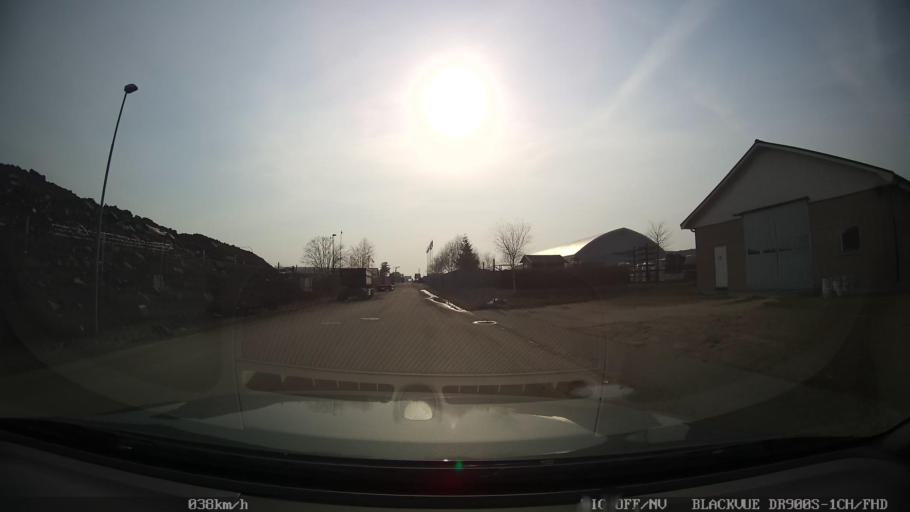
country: SE
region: Skane
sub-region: Ystads Kommun
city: Ystad
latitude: 55.4446
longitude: 13.8538
